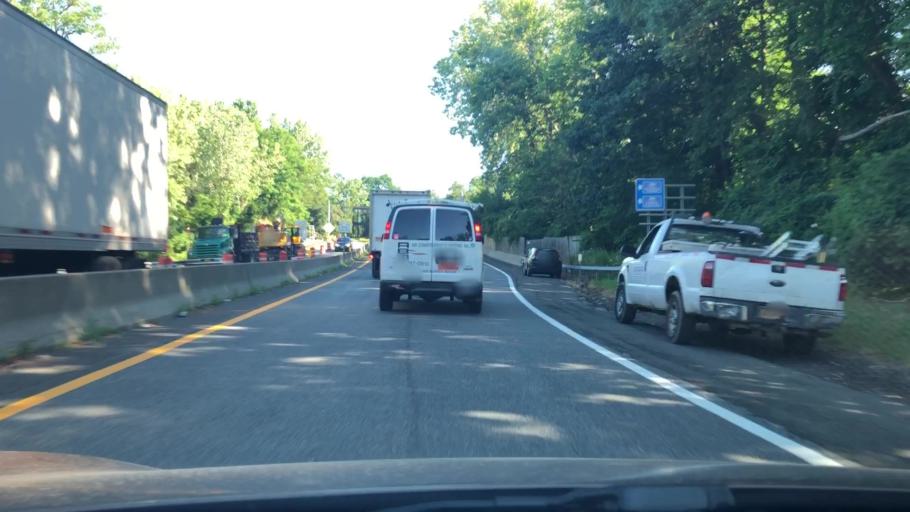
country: US
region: New York
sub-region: Westchester County
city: Tarrytown
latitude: 41.0624
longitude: -73.8571
